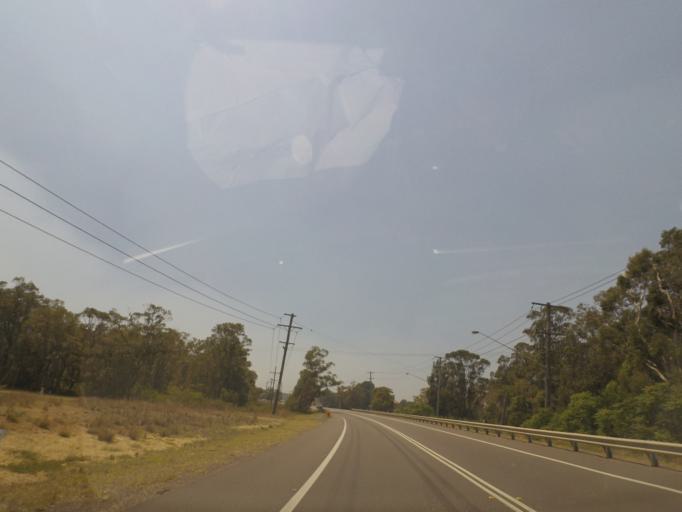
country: AU
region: New South Wales
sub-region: Newcastle
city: Mayfield West
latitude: -32.8324
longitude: 151.7201
